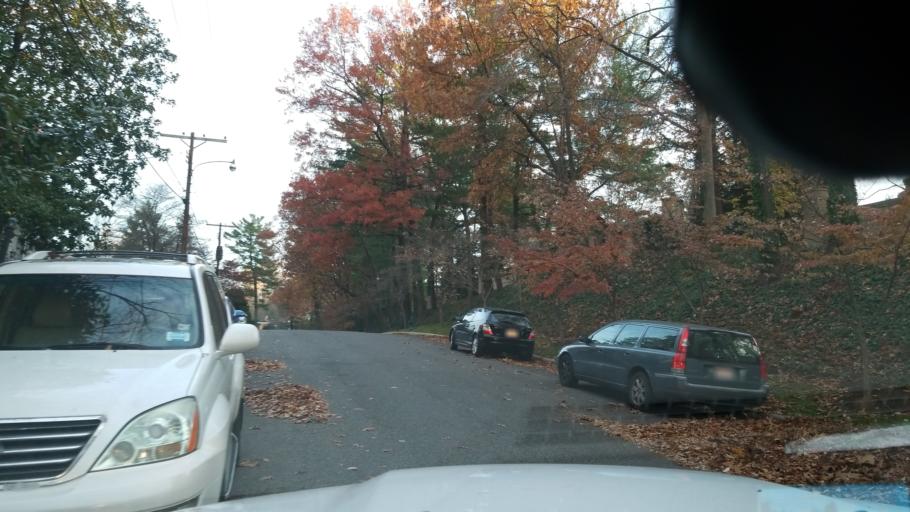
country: US
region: Maryland
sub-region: Montgomery County
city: Brookmont
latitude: 38.9212
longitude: -77.0944
